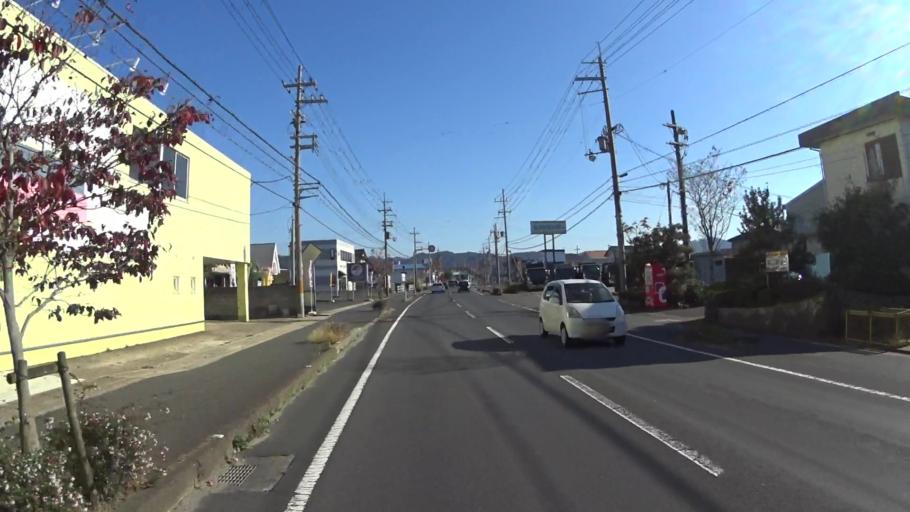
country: JP
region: Kyoto
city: Miyazu
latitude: 35.5945
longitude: 135.0913
